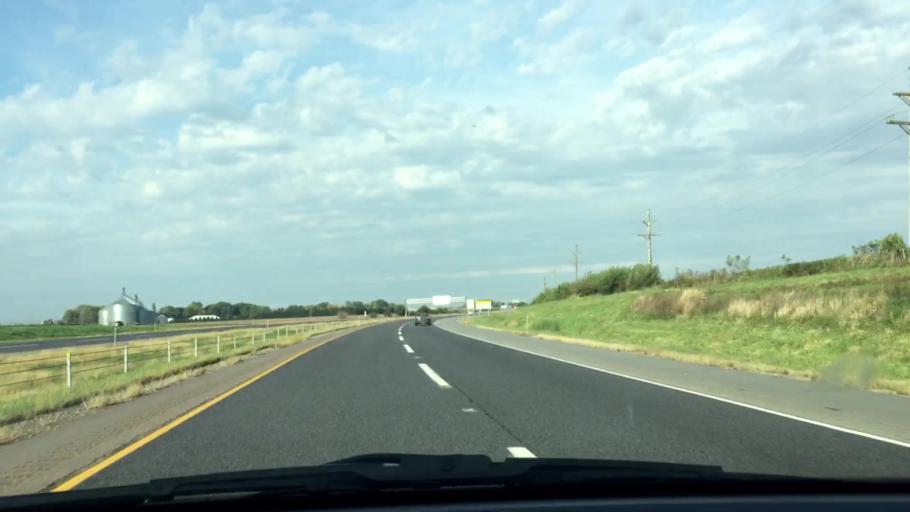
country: US
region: Illinois
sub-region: Lee County
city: Dixon
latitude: 41.8231
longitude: -89.4357
